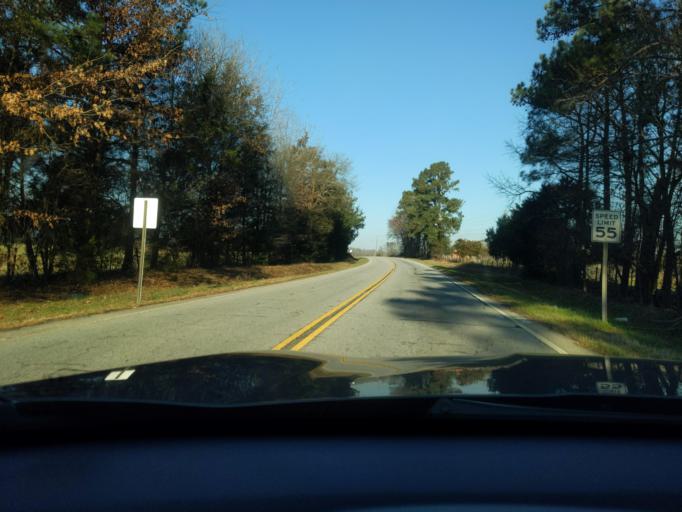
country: US
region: South Carolina
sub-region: Newberry County
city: Newberry
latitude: 34.2211
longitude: -81.7208
